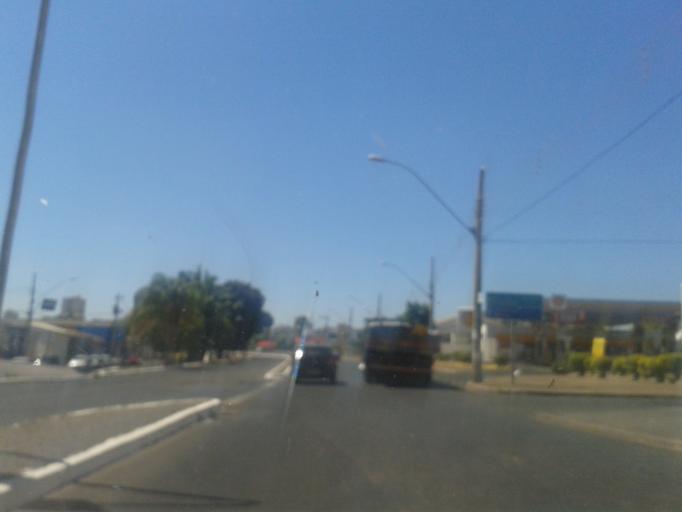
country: BR
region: Minas Gerais
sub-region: Uberlandia
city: Uberlandia
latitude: -18.9002
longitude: -48.2704
